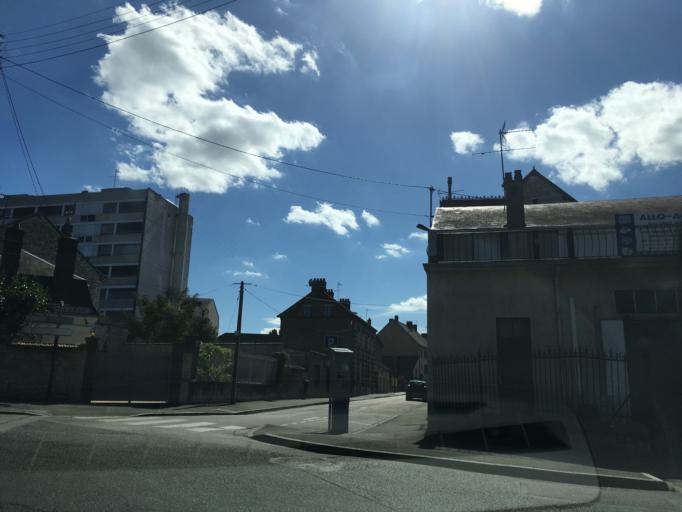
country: FR
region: Haute-Normandie
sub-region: Departement de l'Eure
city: Vernon
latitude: 49.0933
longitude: 1.4818
